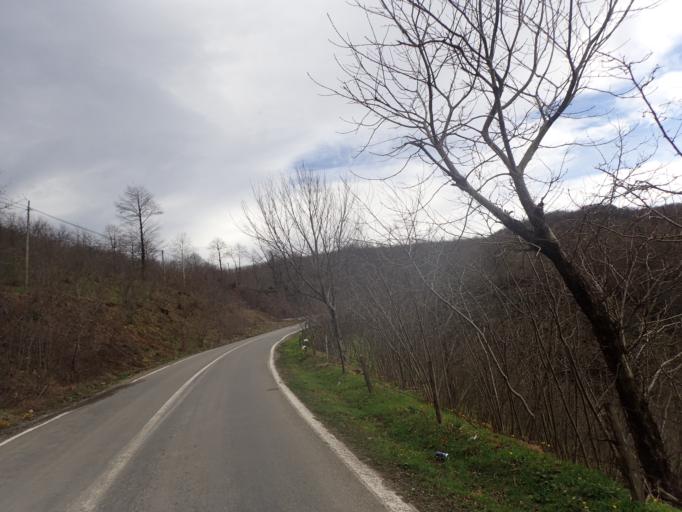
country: TR
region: Ordu
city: Camas
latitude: 40.8879
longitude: 37.5294
